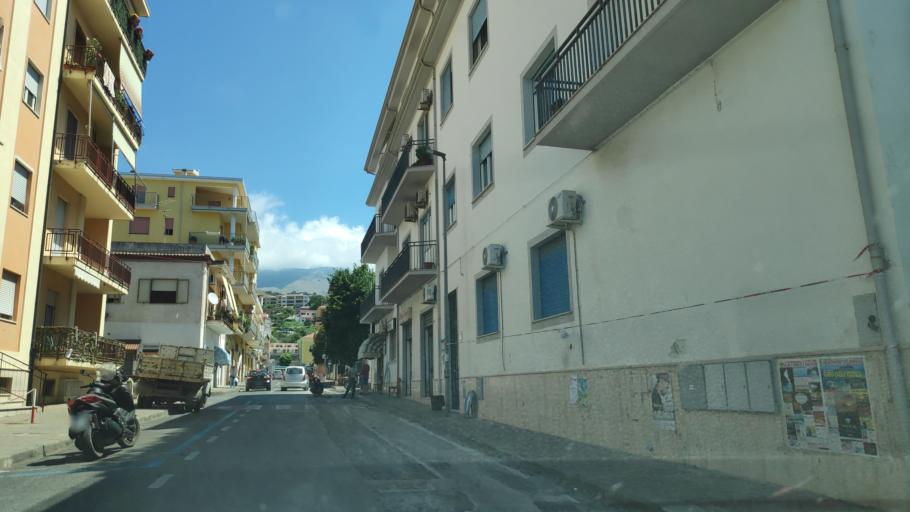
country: IT
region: Calabria
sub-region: Provincia di Cosenza
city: Diamante
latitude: 39.6757
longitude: 15.8222
